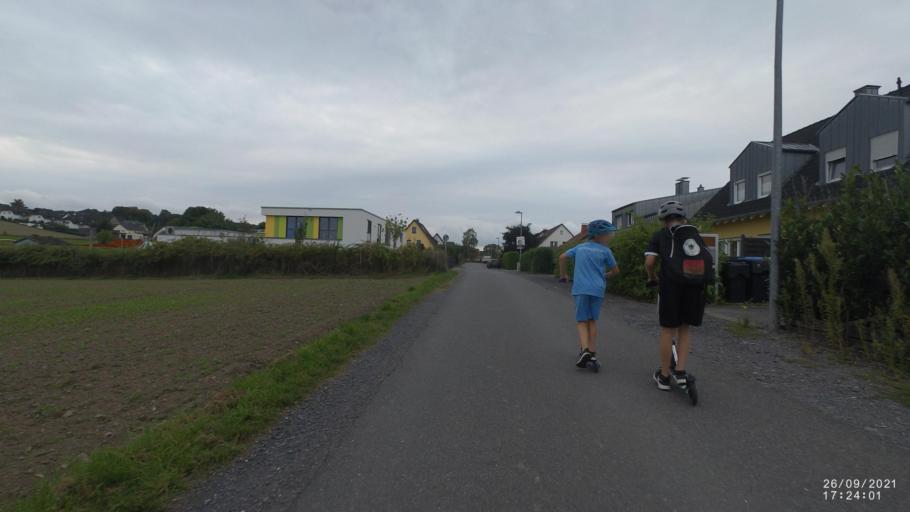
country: DE
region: North Rhine-Westphalia
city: Iserlohn
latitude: 51.4218
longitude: 7.7194
